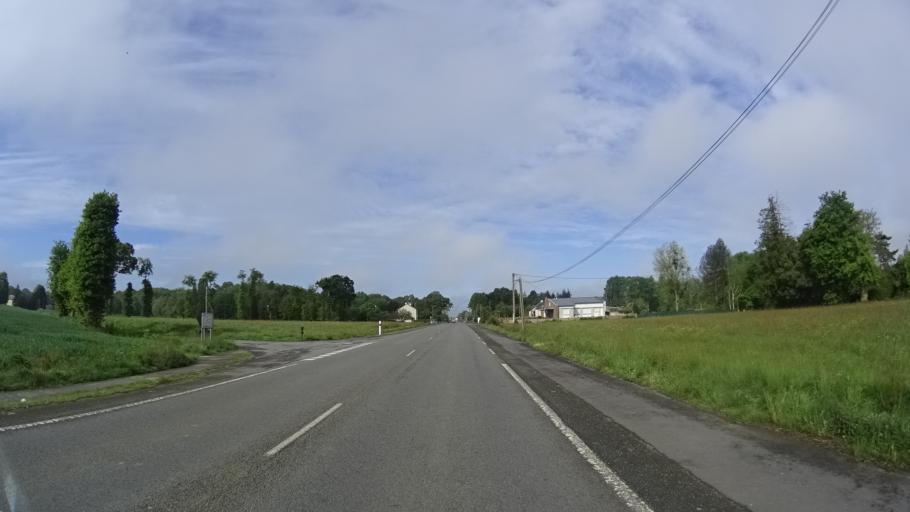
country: FR
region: Brittany
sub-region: Departement d'Ille-et-Vilaine
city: Mordelles
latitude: 48.0826
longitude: -1.8209
